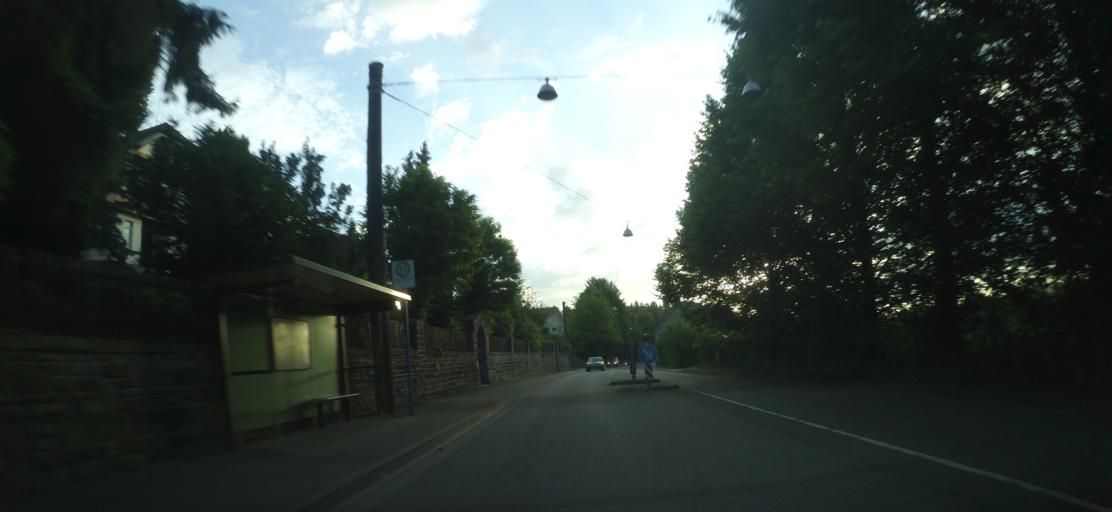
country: DE
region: Saarland
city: Kleinblittersdorf
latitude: 49.1905
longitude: 7.0914
